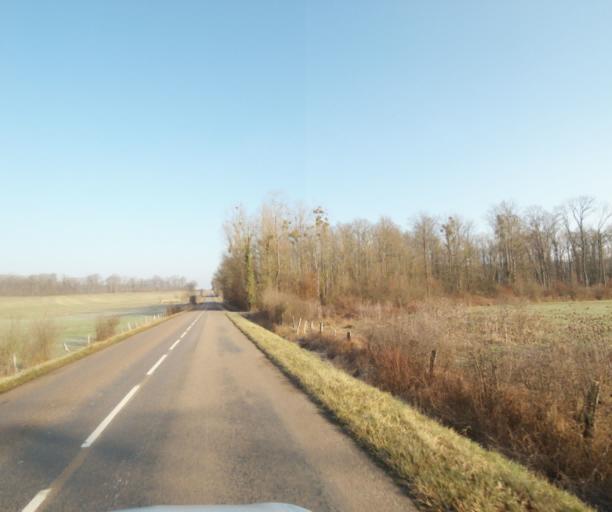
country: FR
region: Champagne-Ardenne
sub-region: Departement de la Haute-Marne
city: Montier-en-Der
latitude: 48.4267
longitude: 4.7492
